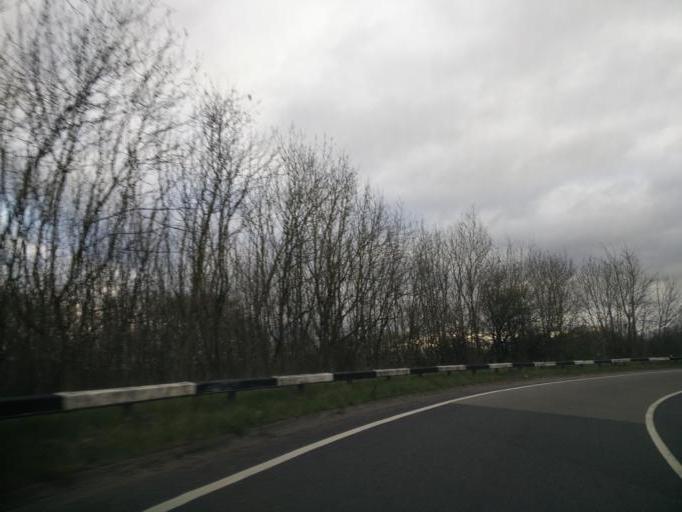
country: GB
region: England
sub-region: County Durham
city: Durham
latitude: 54.7893
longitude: -1.5493
